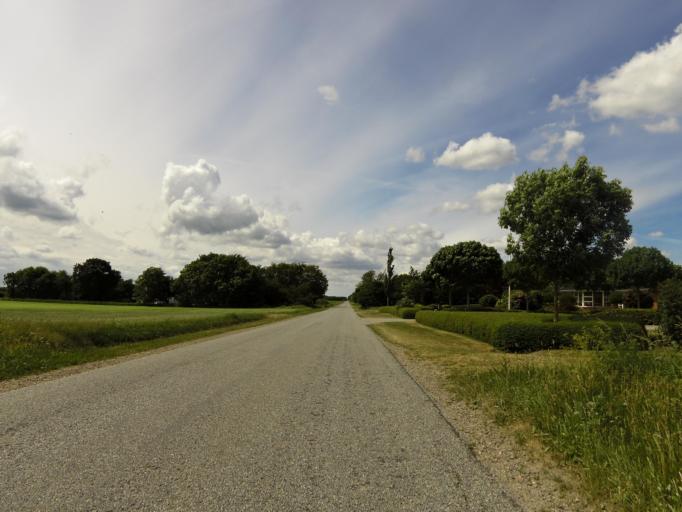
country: DK
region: South Denmark
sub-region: Esbjerg Kommune
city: Ribe
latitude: 55.2627
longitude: 8.8731
